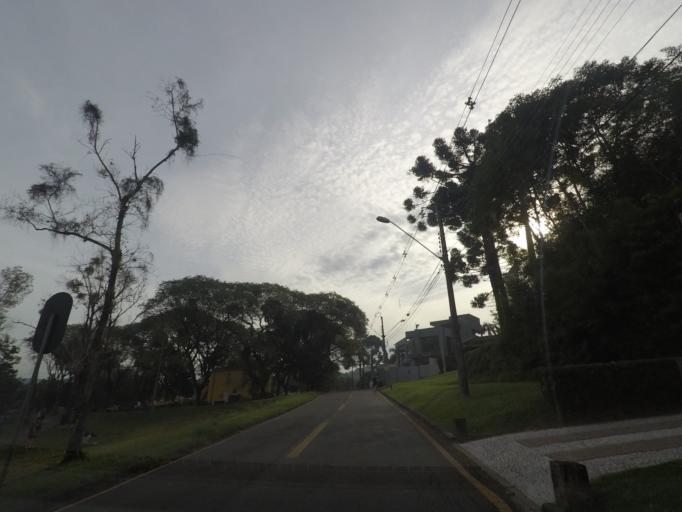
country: BR
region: Parana
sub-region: Curitiba
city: Curitiba
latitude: -25.4248
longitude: -49.3062
